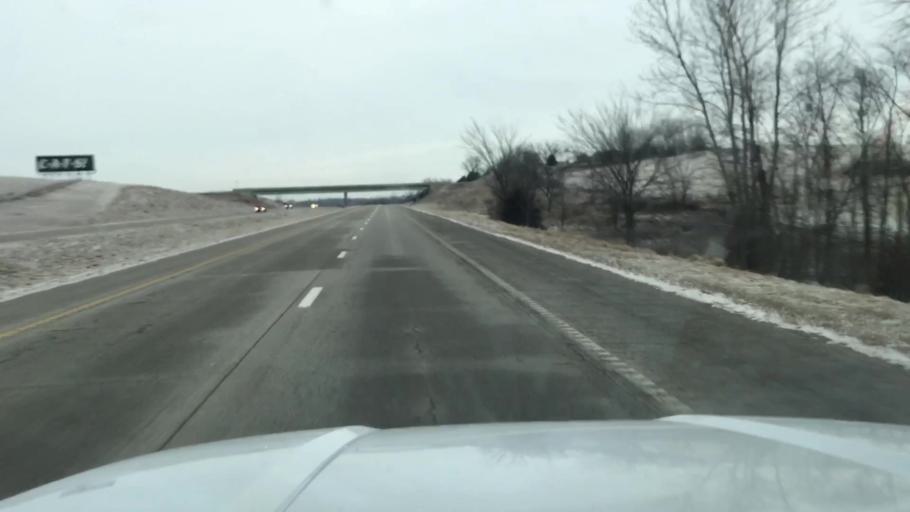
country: US
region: Missouri
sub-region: Andrew County
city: Savannah
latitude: 39.8961
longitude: -94.8570
